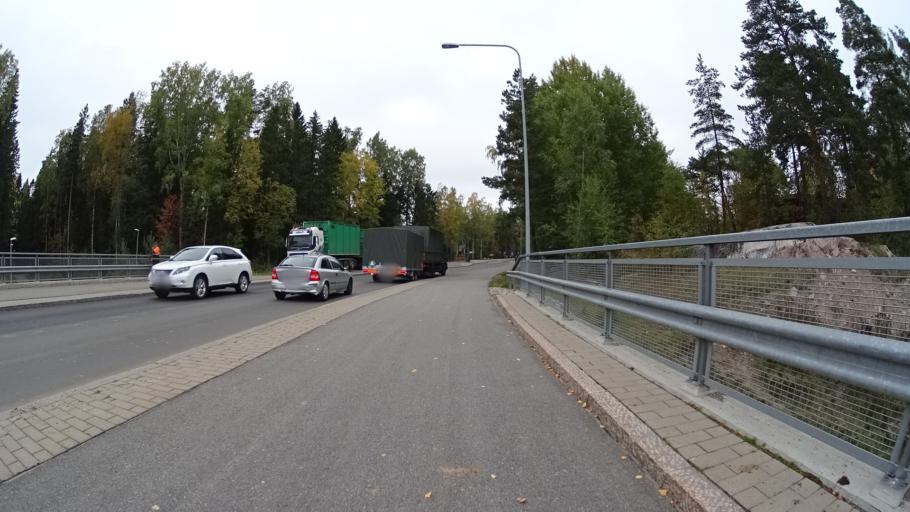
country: FI
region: Uusimaa
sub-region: Helsinki
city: Vantaa
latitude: 60.2191
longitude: 25.0579
